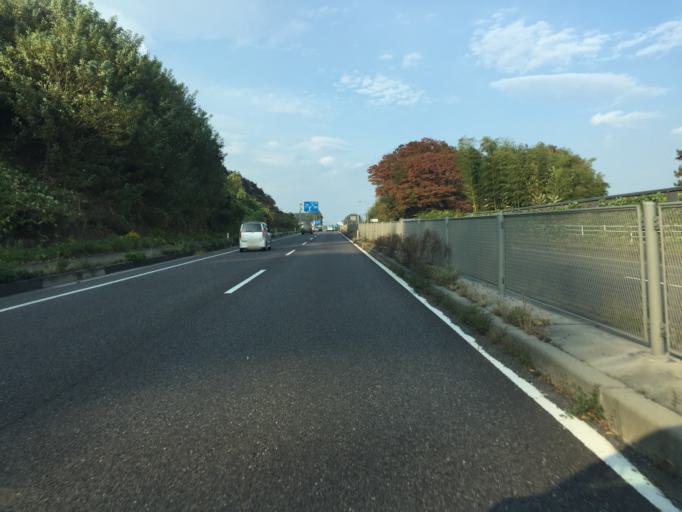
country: JP
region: Fukushima
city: Nihommatsu
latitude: 37.5644
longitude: 140.4114
